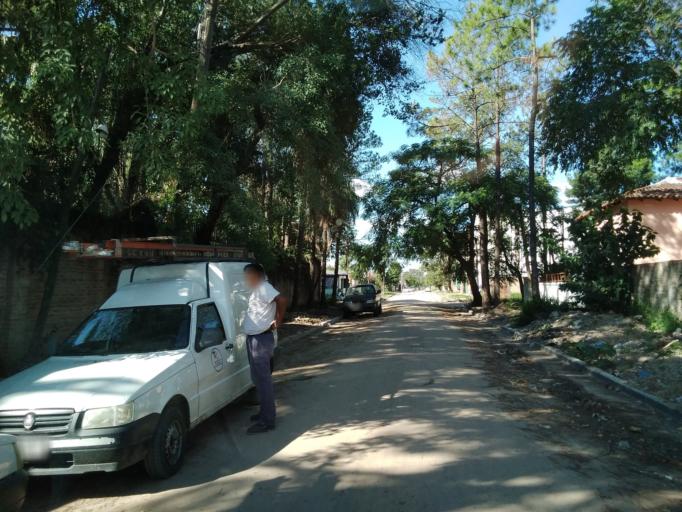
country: AR
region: Corrientes
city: Corrientes
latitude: -27.4649
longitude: -58.7865
